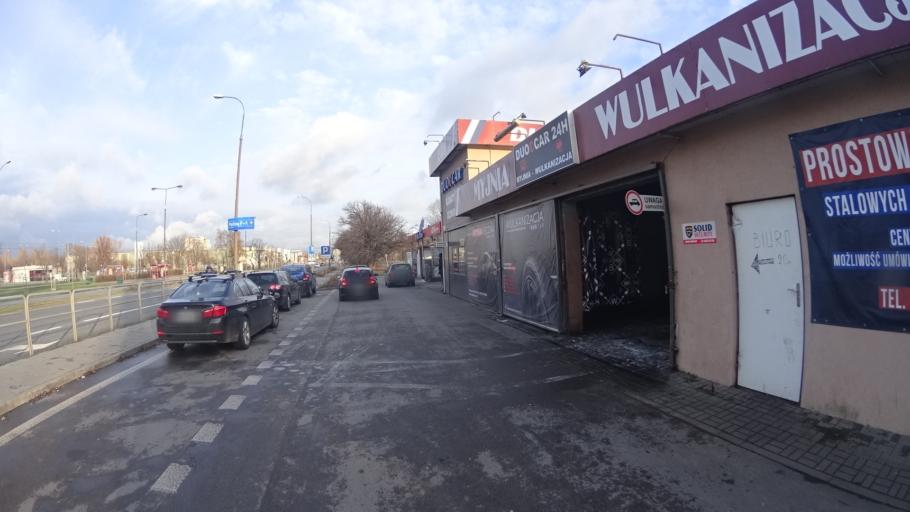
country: PL
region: Masovian Voivodeship
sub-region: Warszawa
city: Bemowo
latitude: 52.2211
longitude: 20.9215
